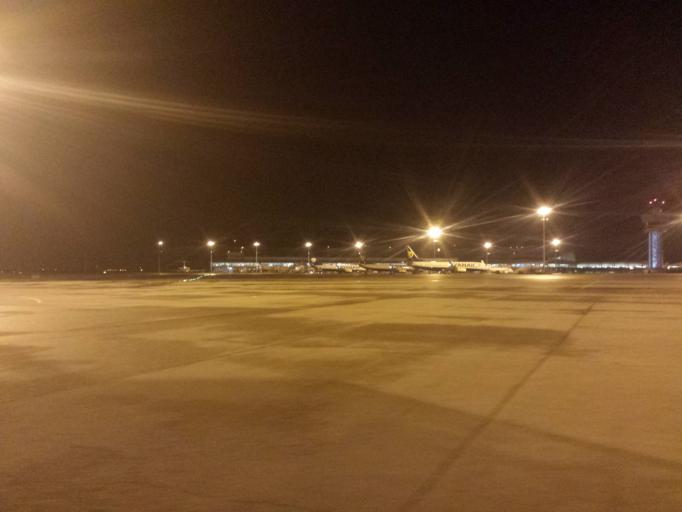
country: BG
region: Sofia-Capital
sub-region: Stolichna Obshtina
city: Sofia
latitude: 42.6902
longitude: 23.4066
